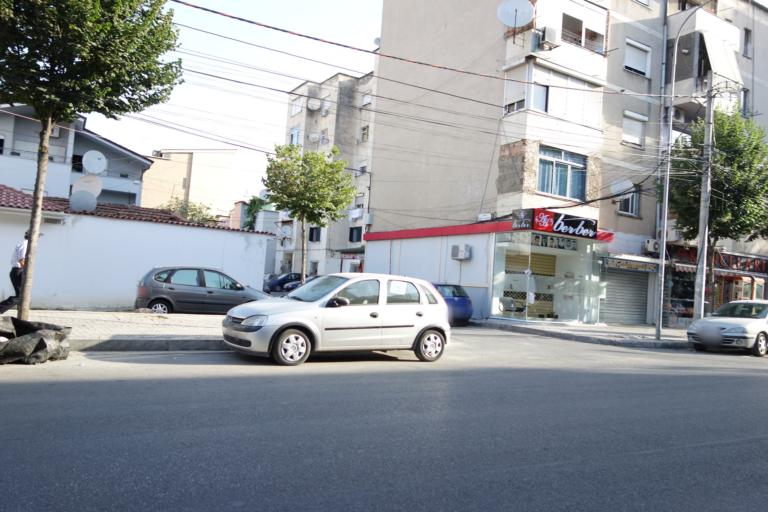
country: AL
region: Tirane
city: Tirana
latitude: 41.3324
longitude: 19.8152
